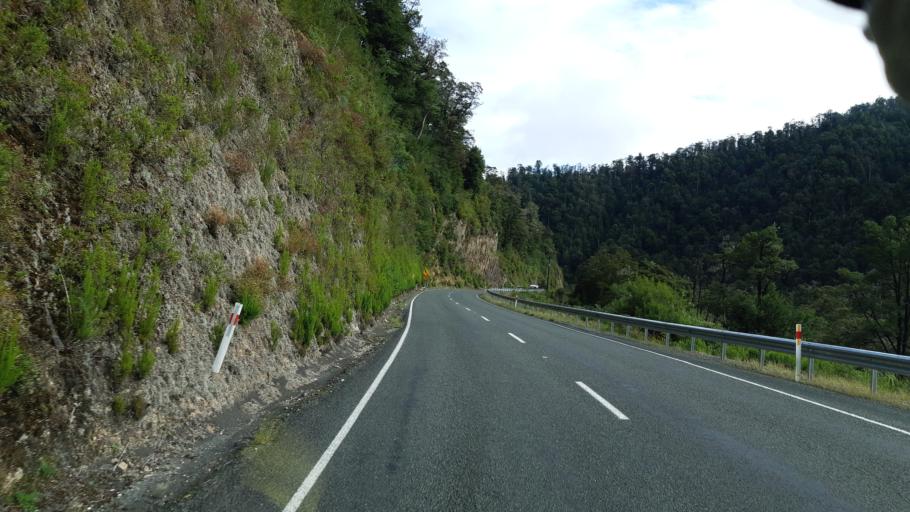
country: NZ
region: West Coast
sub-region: Buller District
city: Westport
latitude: -41.9929
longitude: 172.2203
